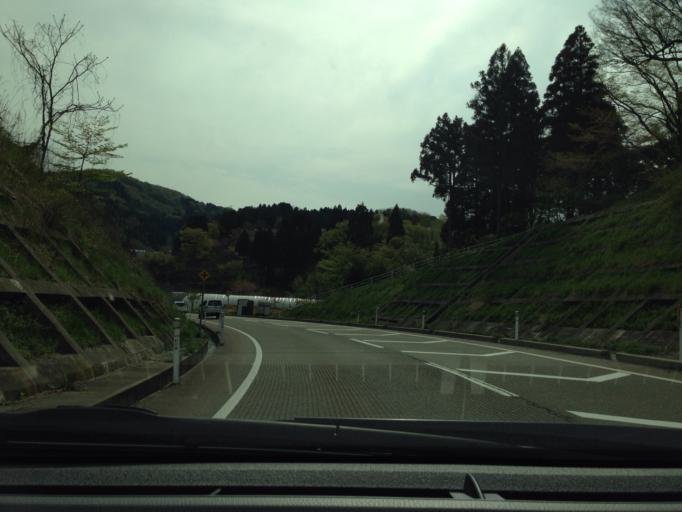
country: JP
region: Toyama
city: Fukumitsu
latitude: 36.5569
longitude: 136.7629
